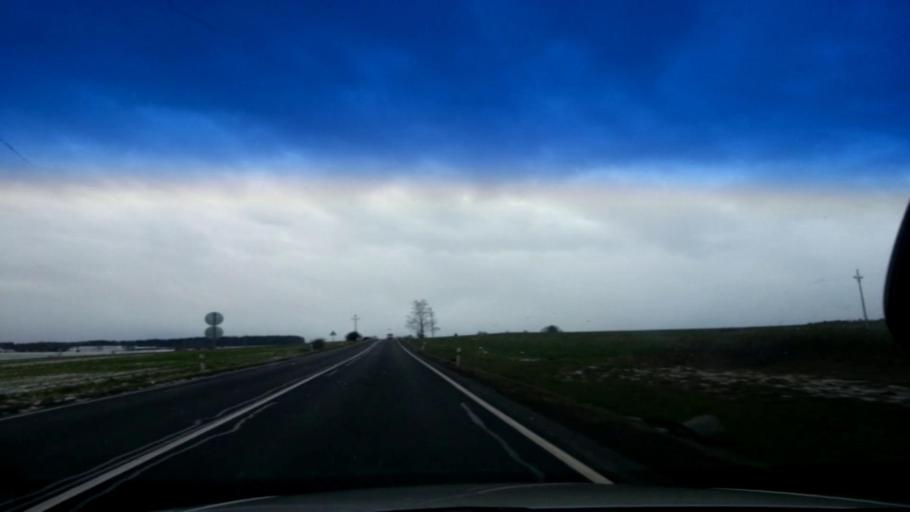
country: CZ
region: Karlovarsky
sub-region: Okres Cheb
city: Frantiskovy Lazne
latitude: 50.1400
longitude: 12.3158
